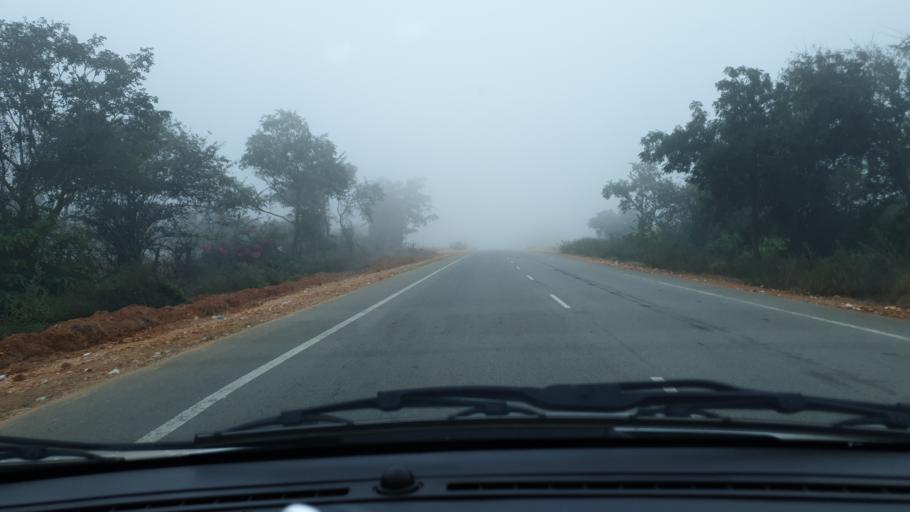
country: IN
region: Telangana
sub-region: Mahbubnagar
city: Nagar Karnul
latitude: 16.6442
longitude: 78.5870
